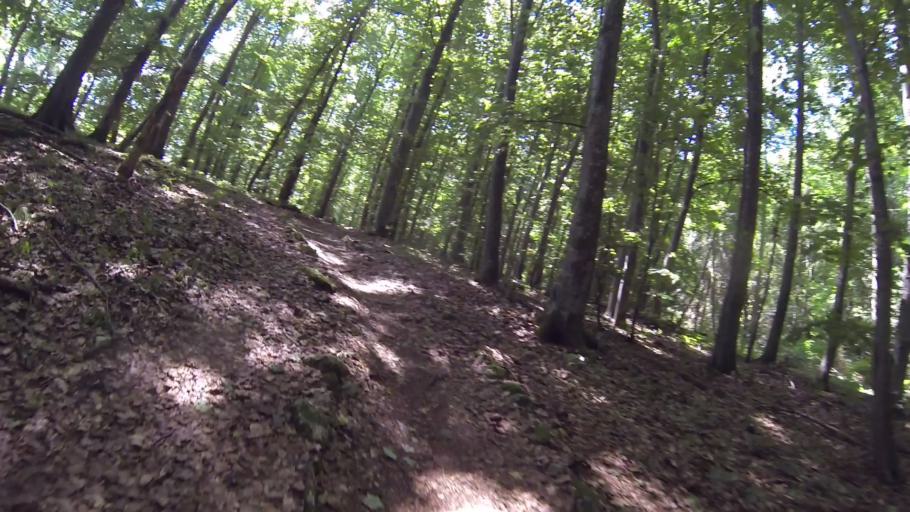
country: DE
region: Baden-Wuerttemberg
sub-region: Regierungsbezirk Stuttgart
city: Herbrechtingen
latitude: 48.6059
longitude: 10.1711
